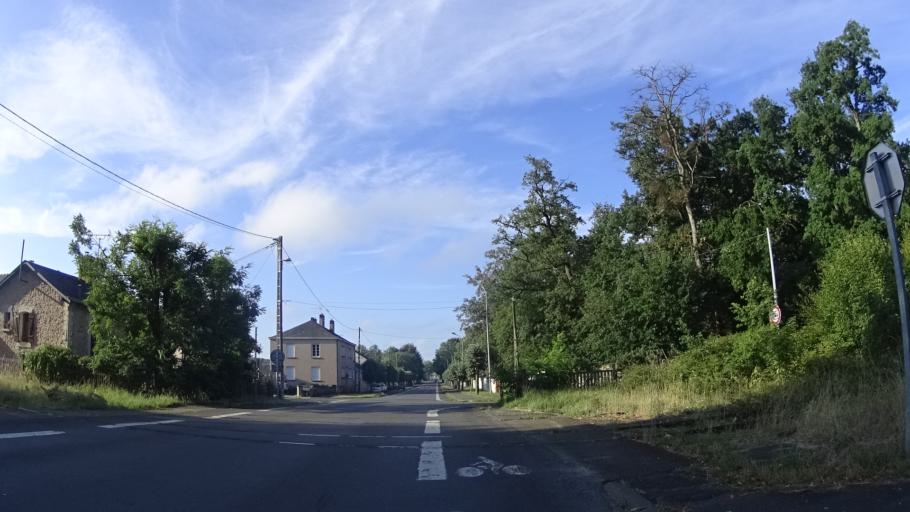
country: FR
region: Pays de la Loire
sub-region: Departement de la Sarthe
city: La Fleche
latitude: 47.6897
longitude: -0.0758
